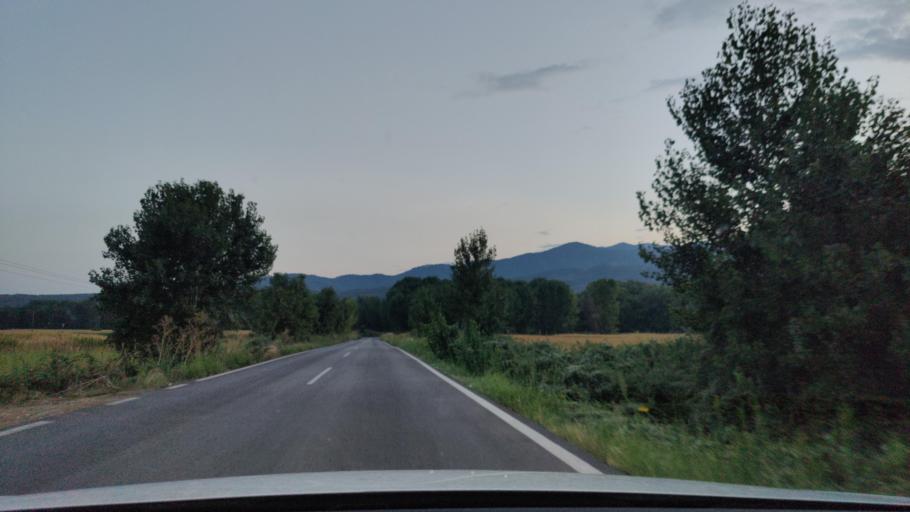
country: GR
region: Central Macedonia
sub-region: Nomos Serron
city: Chrysochorafa
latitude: 41.1450
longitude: 23.2320
